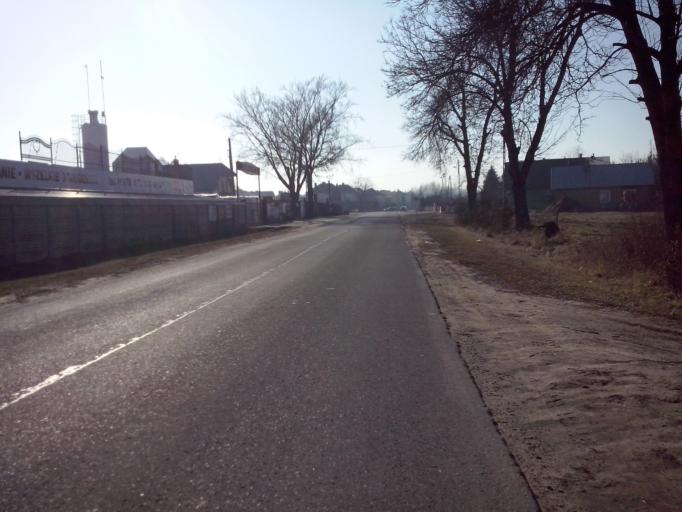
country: PL
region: Subcarpathian Voivodeship
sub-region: Powiat nizanski
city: Krzeszow
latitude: 50.4176
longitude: 22.3514
